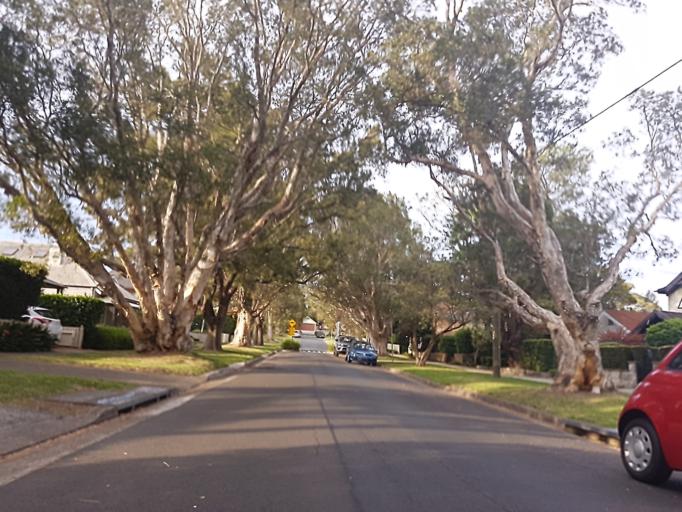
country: AU
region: New South Wales
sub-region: North Sydney
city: St Leonards
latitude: -33.8056
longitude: 151.2032
